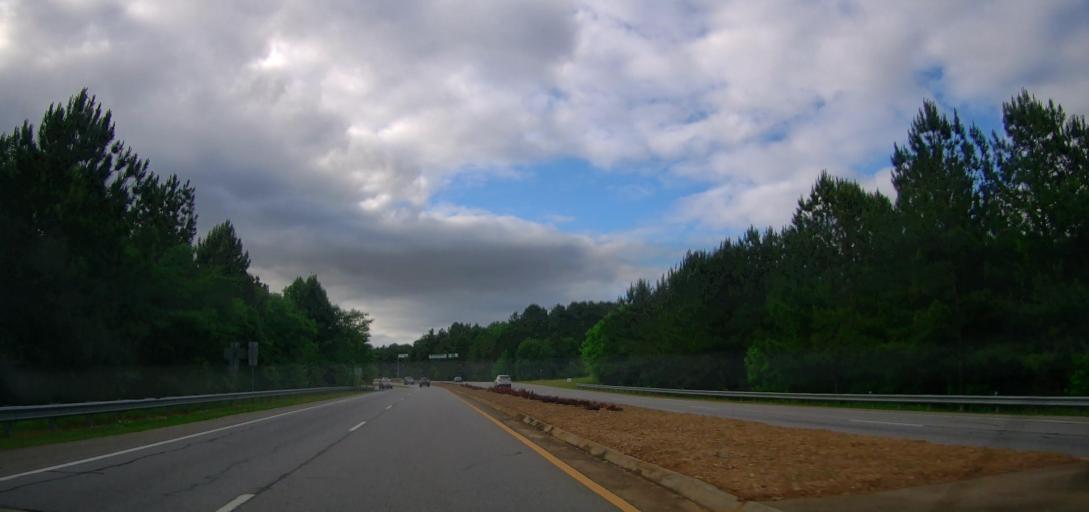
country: US
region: Georgia
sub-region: Clarke County
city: Athens
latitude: 33.9167
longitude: -83.4053
